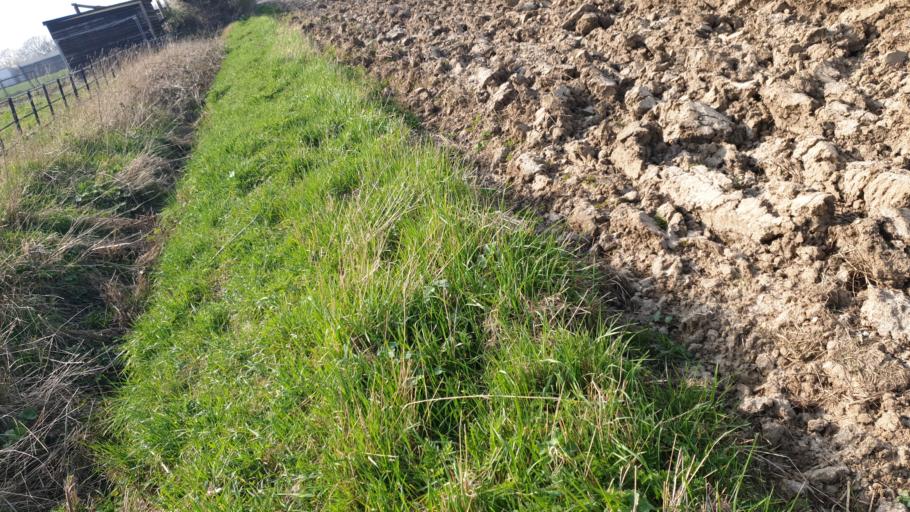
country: GB
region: England
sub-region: Essex
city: Mistley
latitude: 51.9028
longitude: 1.1281
